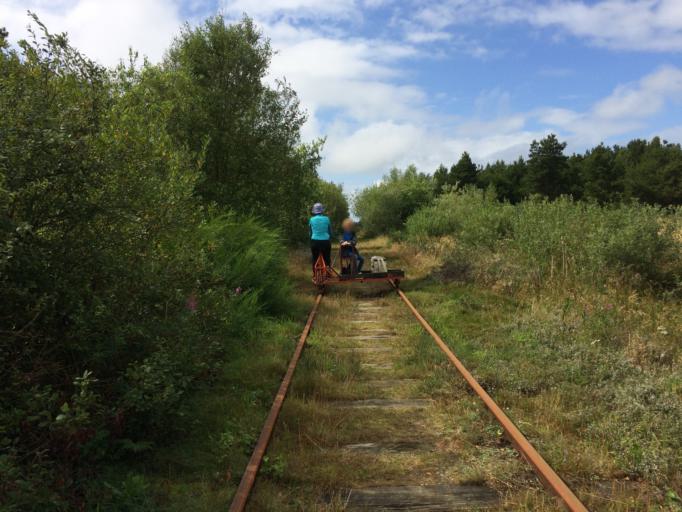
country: DK
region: South Denmark
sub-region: Varde Kommune
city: Oksbol
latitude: 55.7843
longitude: 8.2574
